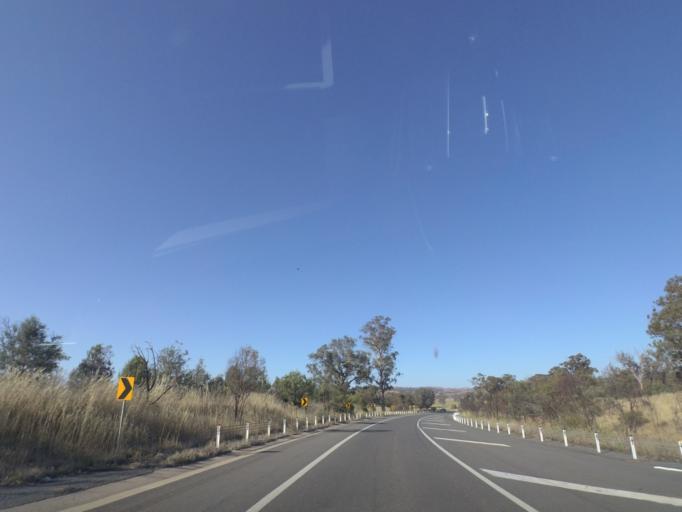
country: AU
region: New South Wales
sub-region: Wagga Wagga
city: Forest Hill
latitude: -35.2609
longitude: 147.7454
